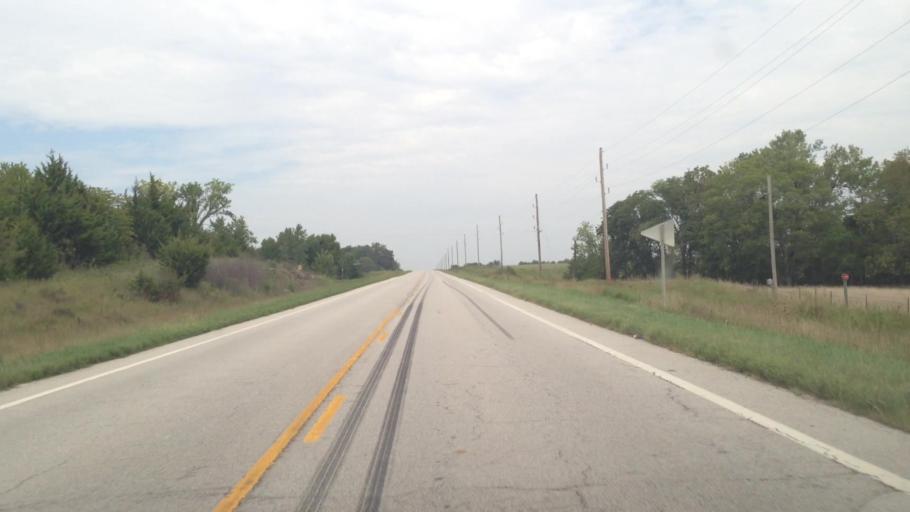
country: US
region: Kansas
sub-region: Allen County
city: Iola
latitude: 37.9637
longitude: -95.1701
